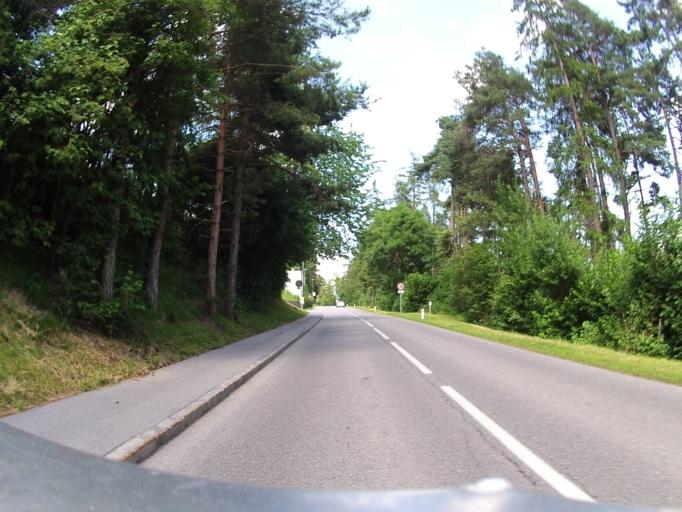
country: AT
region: Tyrol
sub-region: Politischer Bezirk Imst
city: Imst
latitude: 47.2541
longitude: 10.7395
